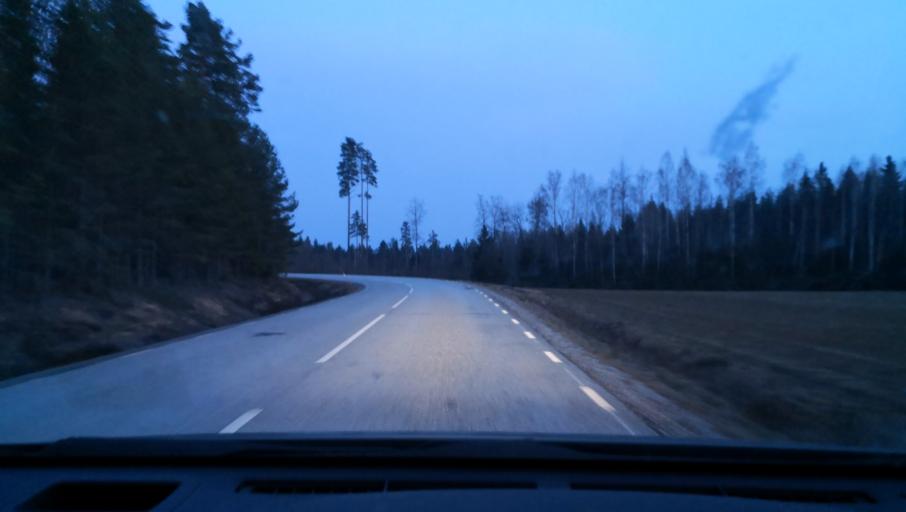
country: SE
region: OErebro
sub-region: Lindesbergs Kommun
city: Frovi
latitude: 59.5871
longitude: 15.4385
